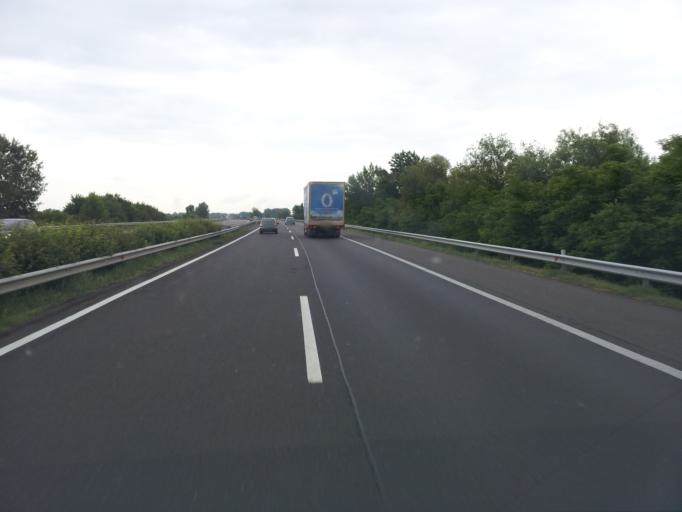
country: HU
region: Heves
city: Kompolt
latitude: 47.7116
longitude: 20.2333
